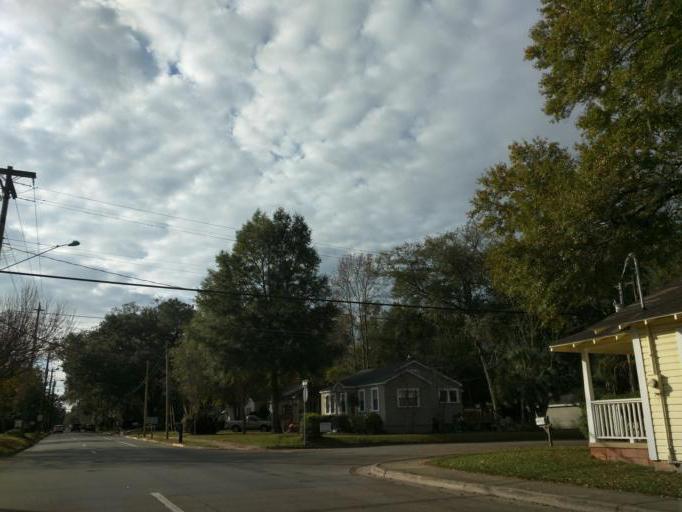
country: US
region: Florida
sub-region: Leon County
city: Tallahassee
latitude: 30.4594
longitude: -84.2844
